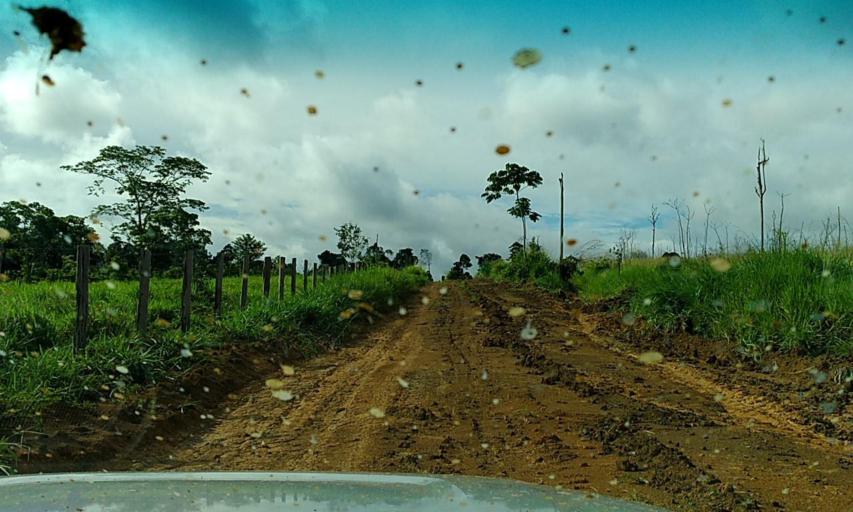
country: BR
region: Para
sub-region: Senador Jose Porfirio
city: Senador Jose Porfirio
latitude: -3.0015
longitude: -51.7398
